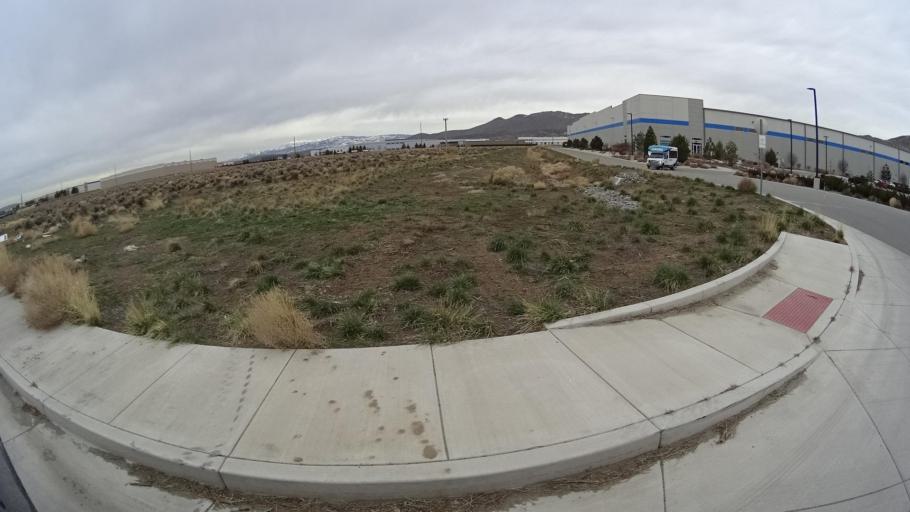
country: US
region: Nevada
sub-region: Washoe County
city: Spanish Springs
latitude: 39.6802
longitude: -119.7057
